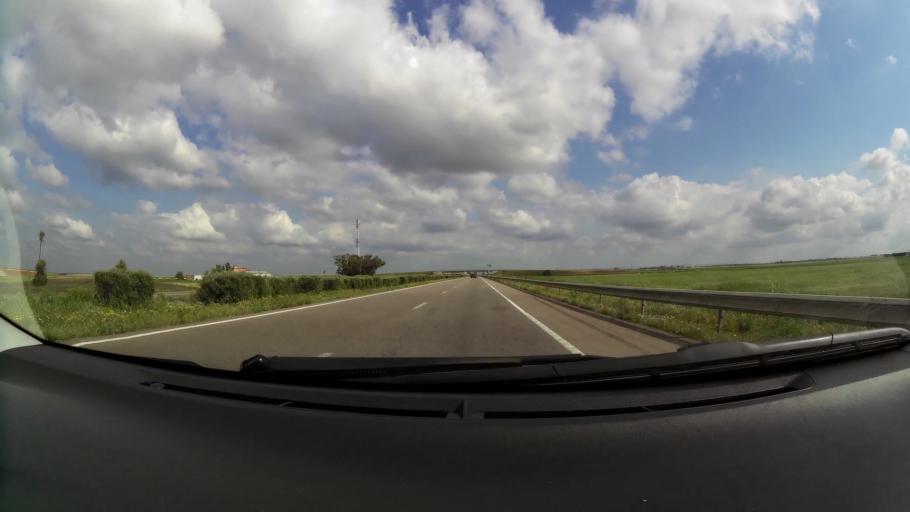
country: MA
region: Chaouia-Ouardigha
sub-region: Settat Province
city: Berrechid
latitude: 33.2930
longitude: -7.5531
